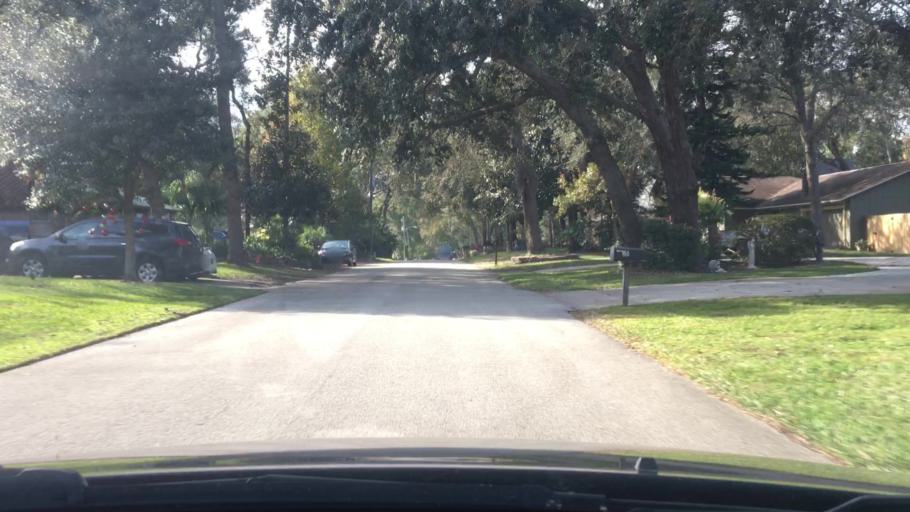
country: US
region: Florida
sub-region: Volusia County
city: Ormond Beach
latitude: 29.2741
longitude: -81.1015
